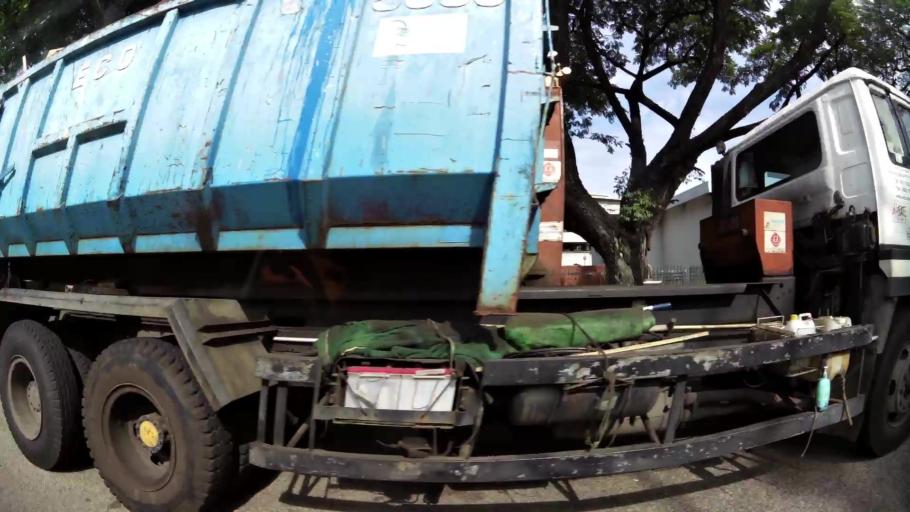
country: MY
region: Johor
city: Johor Bahru
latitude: 1.3108
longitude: 103.6523
